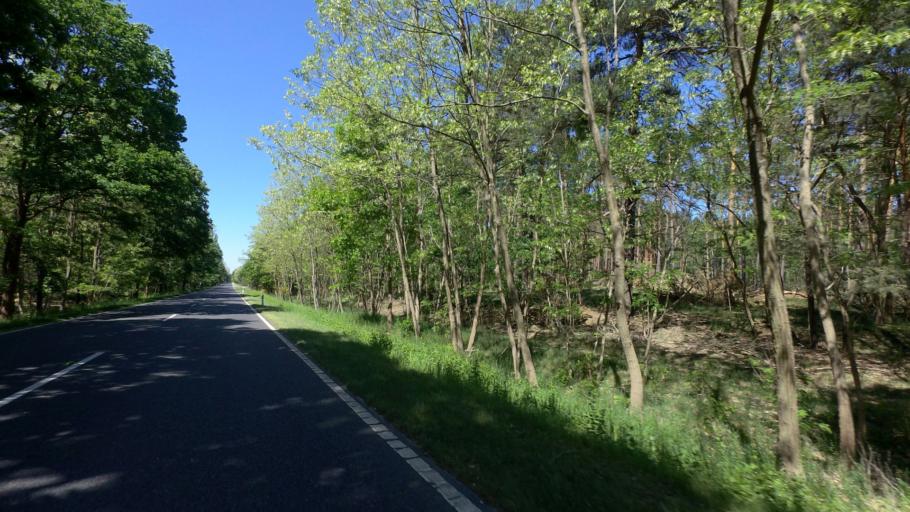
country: DE
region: Brandenburg
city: Lieberose
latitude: 51.9597
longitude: 14.3240
